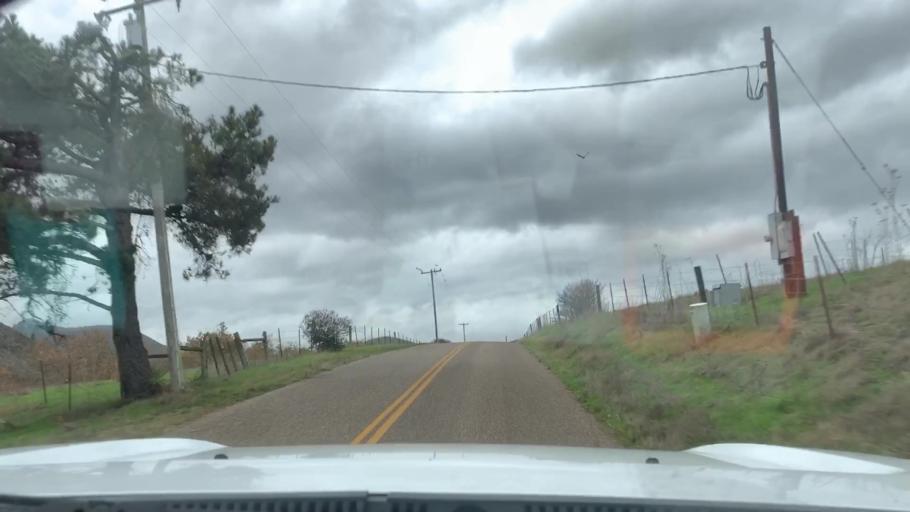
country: US
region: California
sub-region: San Luis Obispo County
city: Morro Bay
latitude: 35.3768
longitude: -120.7911
